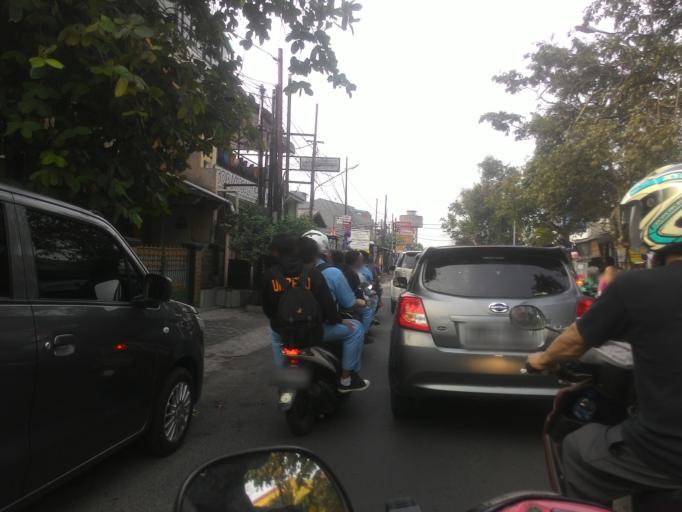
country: ID
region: West Java
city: Depok
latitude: -6.3868
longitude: 106.8143
